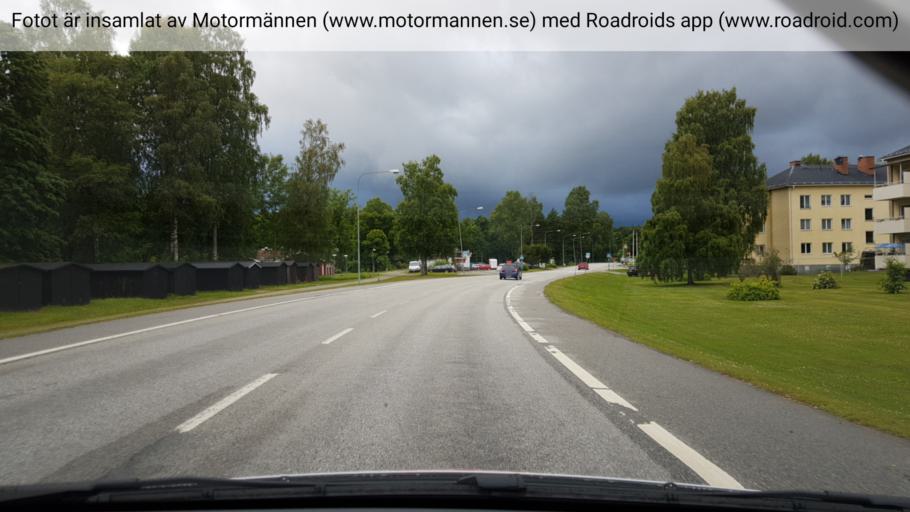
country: SE
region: OErebro
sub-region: Ljusnarsbergs Kommun
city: Kopparberg
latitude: 59.8719
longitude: 15.0066
